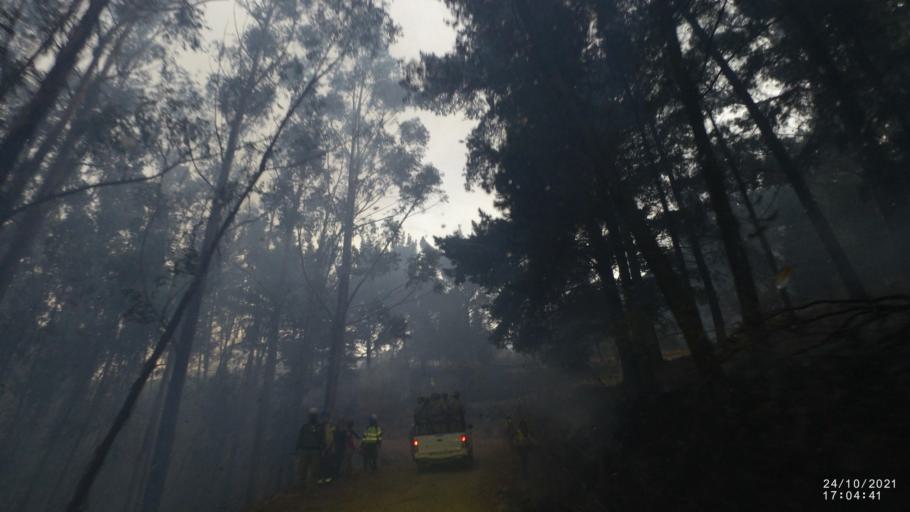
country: BO
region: Cochabamba
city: Cochabamba
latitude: -17.3353
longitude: -66.1407
